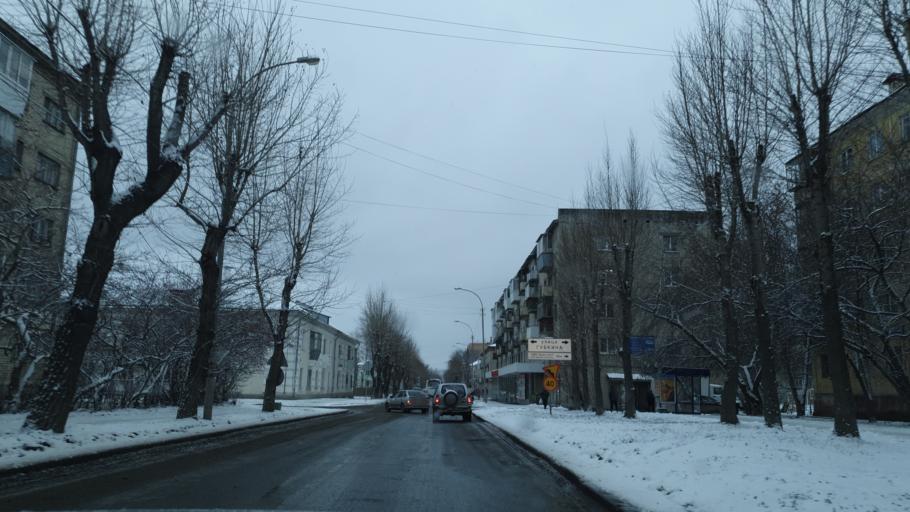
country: RU
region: Sverdlovsk
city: Istok
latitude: 56.7513
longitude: 60.7091
